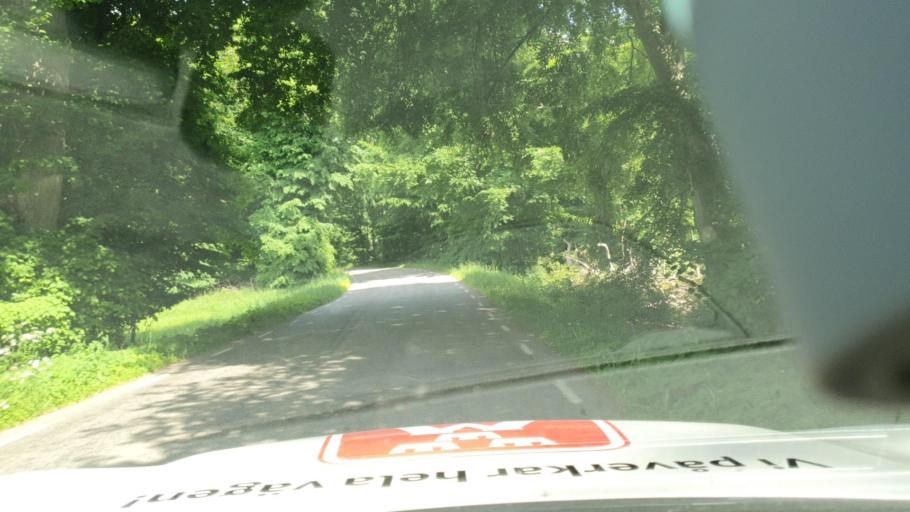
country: SE
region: Skane
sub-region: Svedala Kommun
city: Svedala
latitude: 55.5341
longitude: 13.2243
